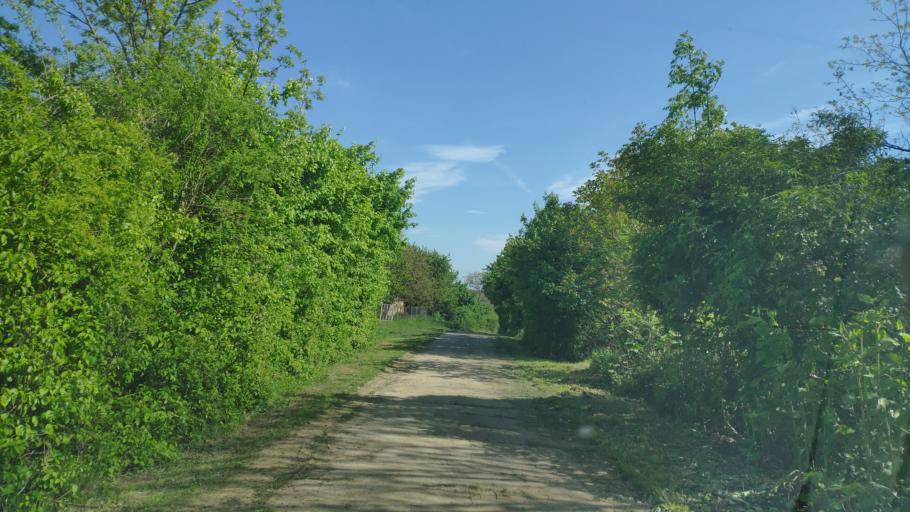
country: SK
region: Kosicky
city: Secovce
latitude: 48.6857
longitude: 21.6077
